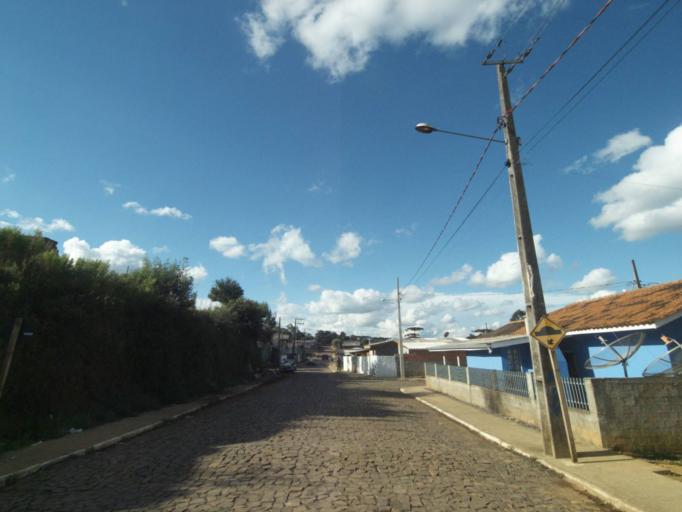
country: BR
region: Parana
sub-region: Uniao Da Vitoria
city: Uniao da Vitoria
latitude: -26.1618
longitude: -51.5334
